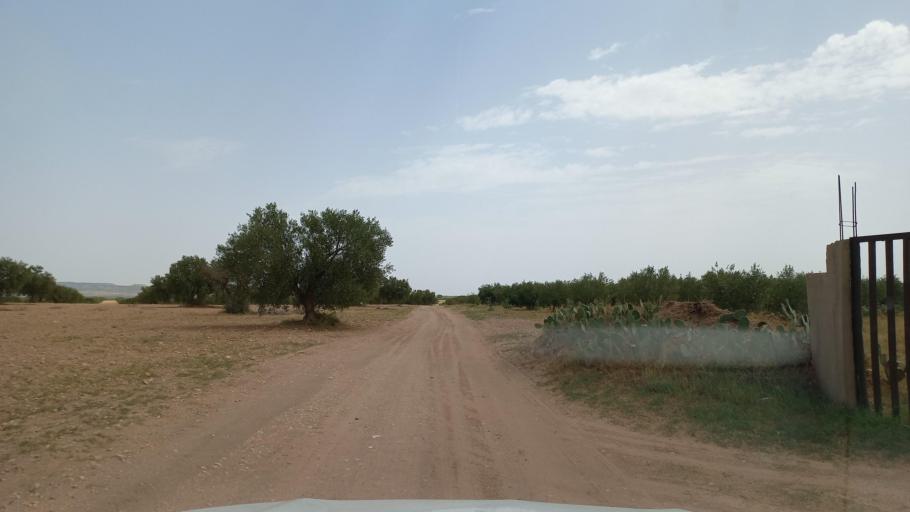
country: TN
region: Al Qasrayn
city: Kasserine
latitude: 35.2902
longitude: 9.0231
